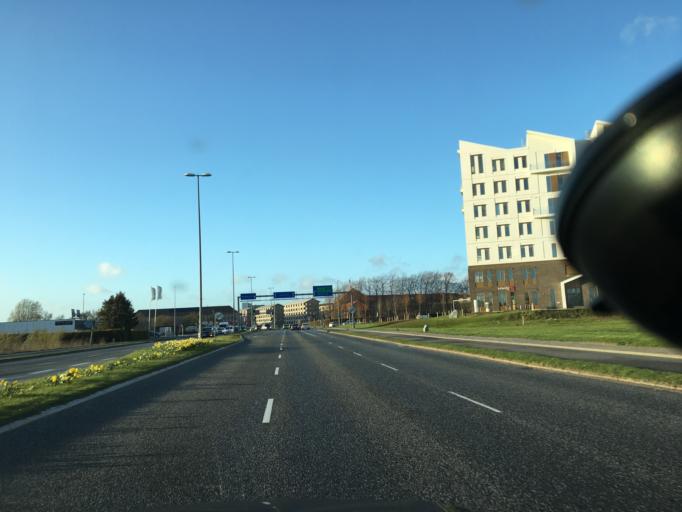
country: DK
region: North Denmark
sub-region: Alborg Kommune
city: Aalborg
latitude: 57.0363
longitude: 9.9312
